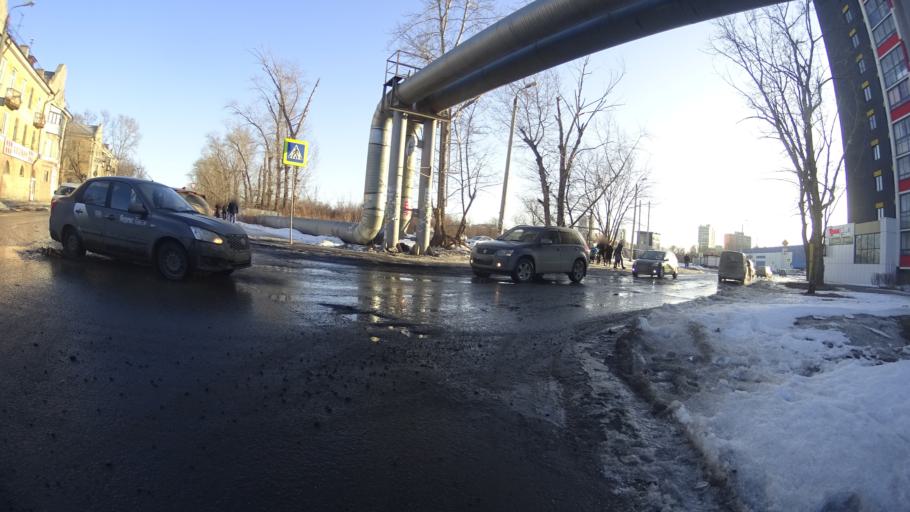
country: RU
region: Chelyabinsk
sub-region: Gorod Chelyabinsk
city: Chelyabinsk
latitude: 55.1359
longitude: 61.4561
